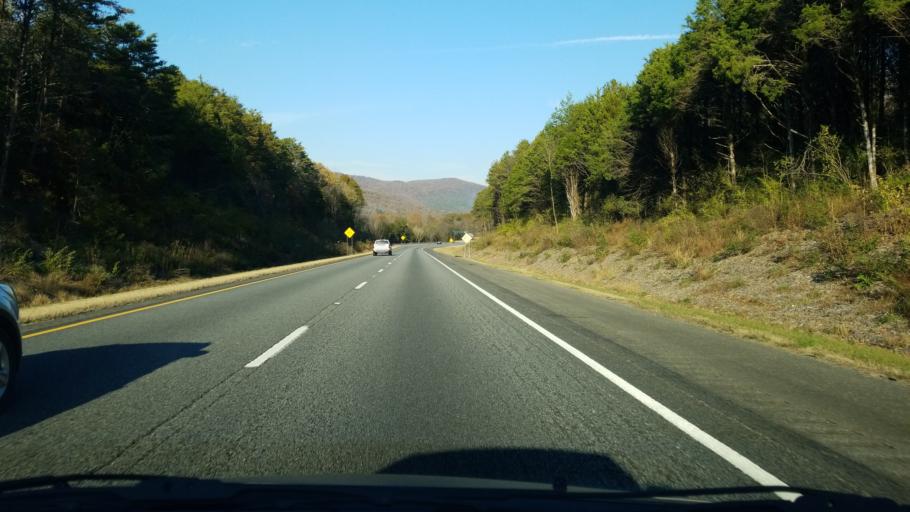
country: US
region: Georgia
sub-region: Walker County
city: Lookout Mountain
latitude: 34.9676
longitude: -85.4506
